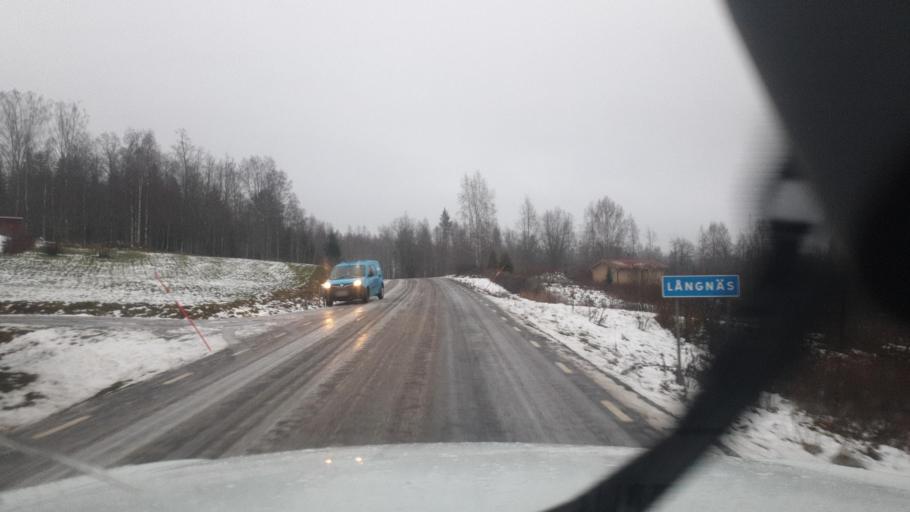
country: SE
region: Vaermland
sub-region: Torsby Kommun
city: Torsby
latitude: 59.9863
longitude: 12.7585
